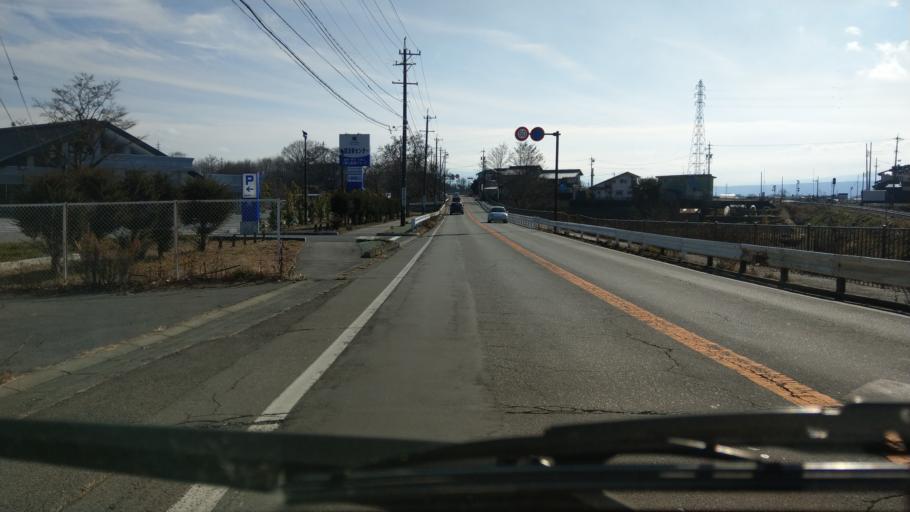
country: JP
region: Nagano
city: Komoro
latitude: 36.3099
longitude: 138.4432
